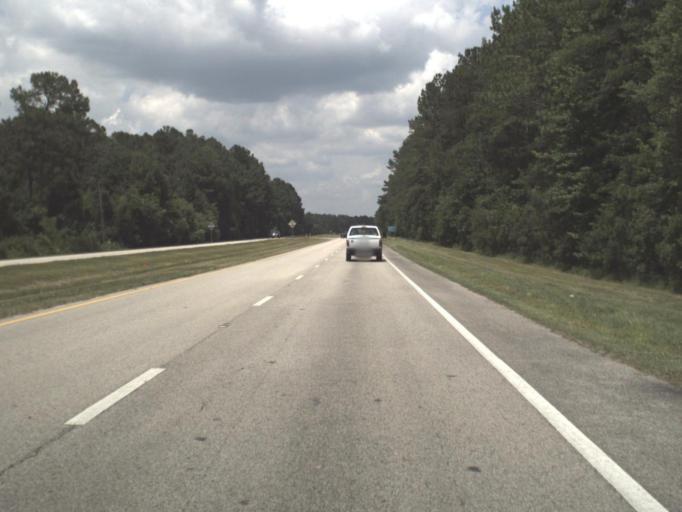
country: US
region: Florida
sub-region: Alachua County
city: Gainesville
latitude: 29.7083
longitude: -82.2733
